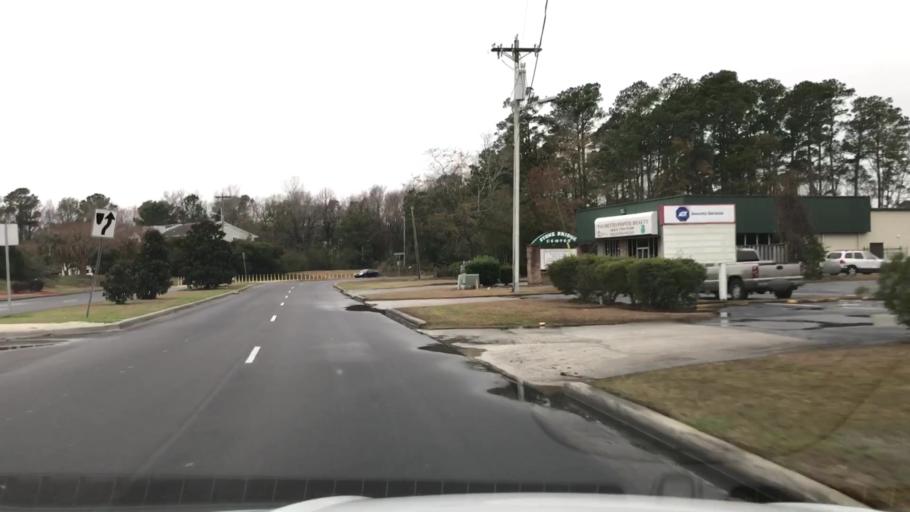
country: US
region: South Carolina
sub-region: Horry County
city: Socastee
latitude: 33.6790
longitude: -78.9666
